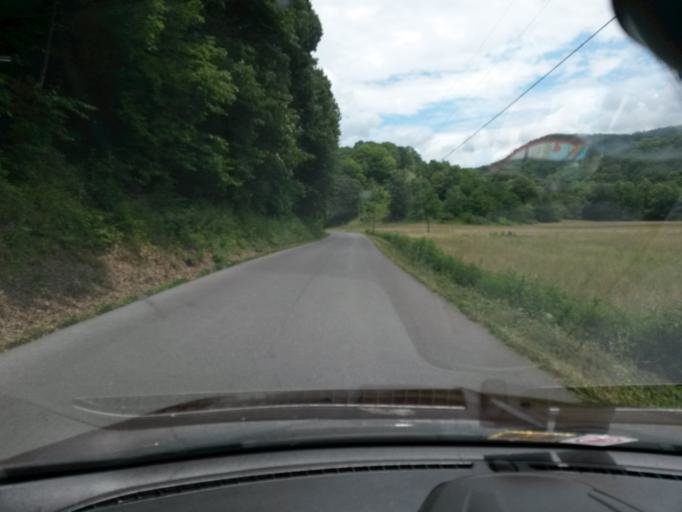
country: US
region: West Virginia
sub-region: Monroe County
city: Union
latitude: 37.5093
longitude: -80.5725
